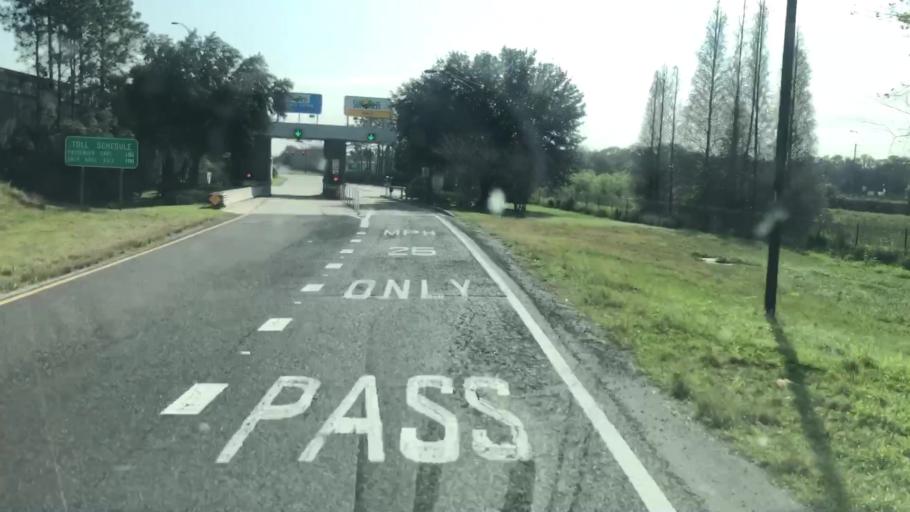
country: US
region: Florida
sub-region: Polk County
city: Winston
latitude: 27.9990
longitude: -82.0008
